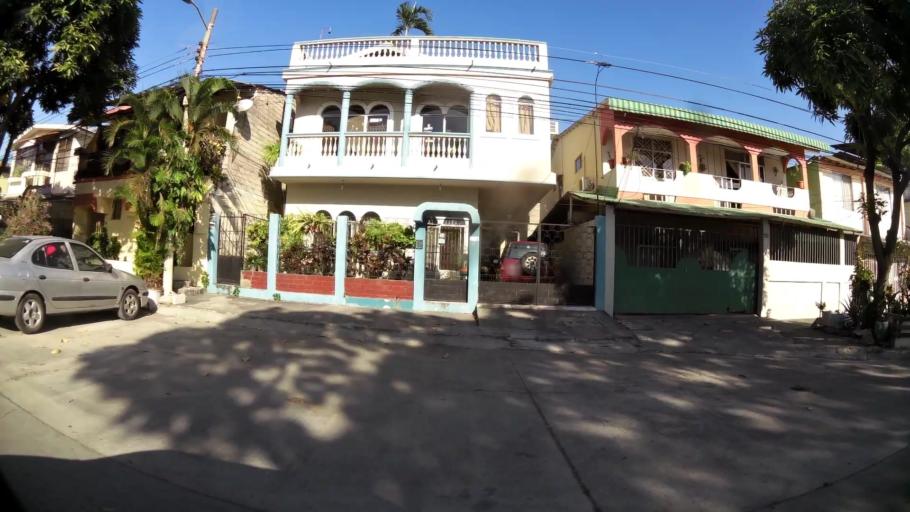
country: EC
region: Guayas
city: Eloy Alfaro
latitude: -2.1680
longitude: -79.8871
